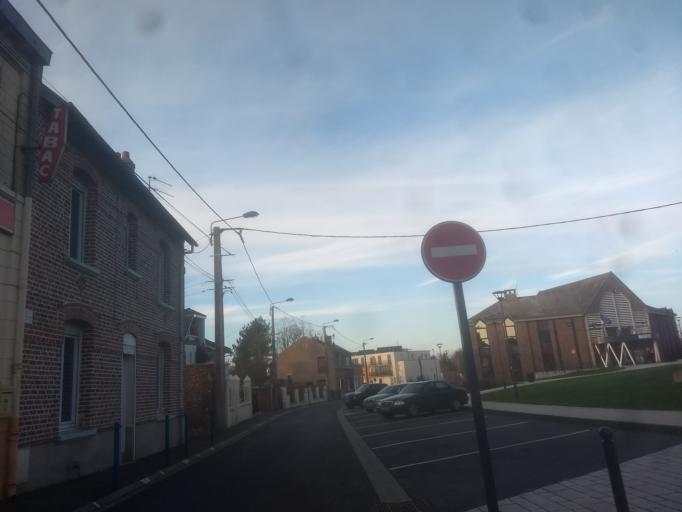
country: FR
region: Nord-Pas-de-Calais
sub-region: Departement du Pas-de-Calais
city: Beaurains
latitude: 50.2626
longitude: 2.7884
